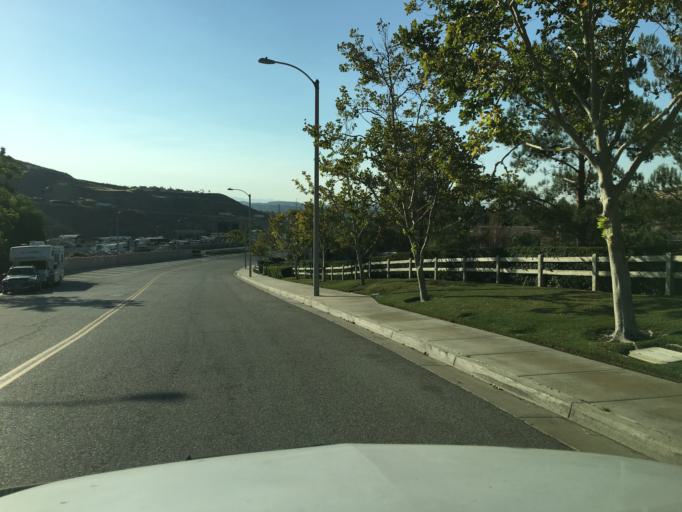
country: US
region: California
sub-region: Los Angeles County
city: Castaic
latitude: 34.5086
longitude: -118.6349
